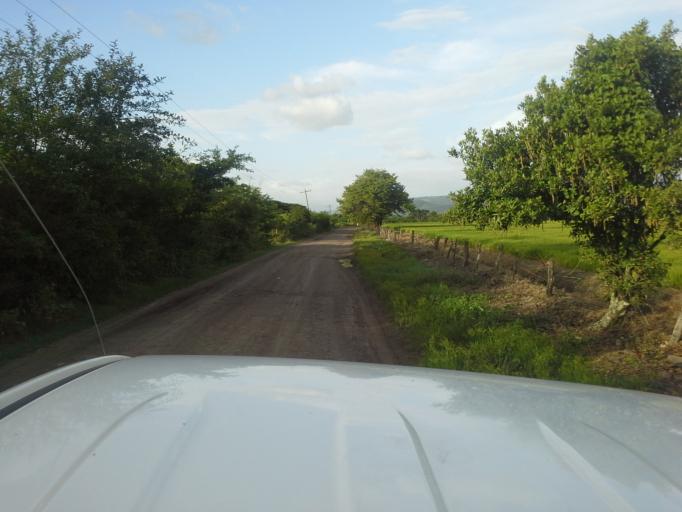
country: NI
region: Matagalpa
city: Ciudad Dario
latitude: 12.7924
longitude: -86.1522
